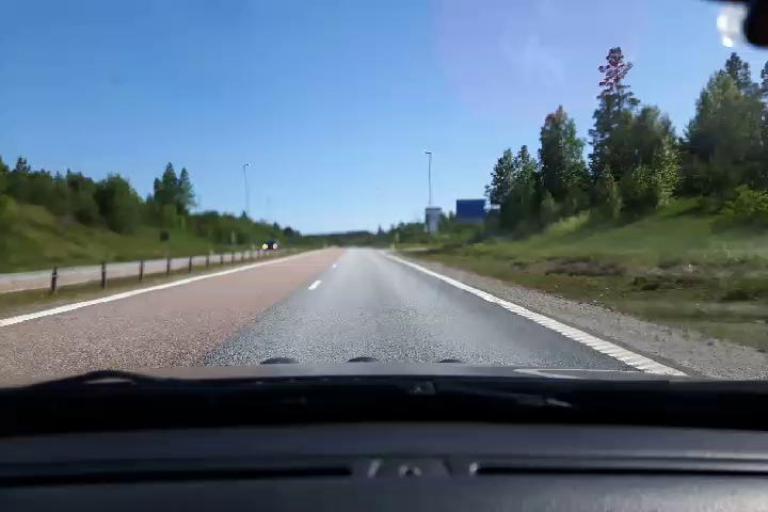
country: SE
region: Gaevleborg
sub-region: Hudiksvalls Kommun
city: Iggesund
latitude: 61.5204
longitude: 16.9772
